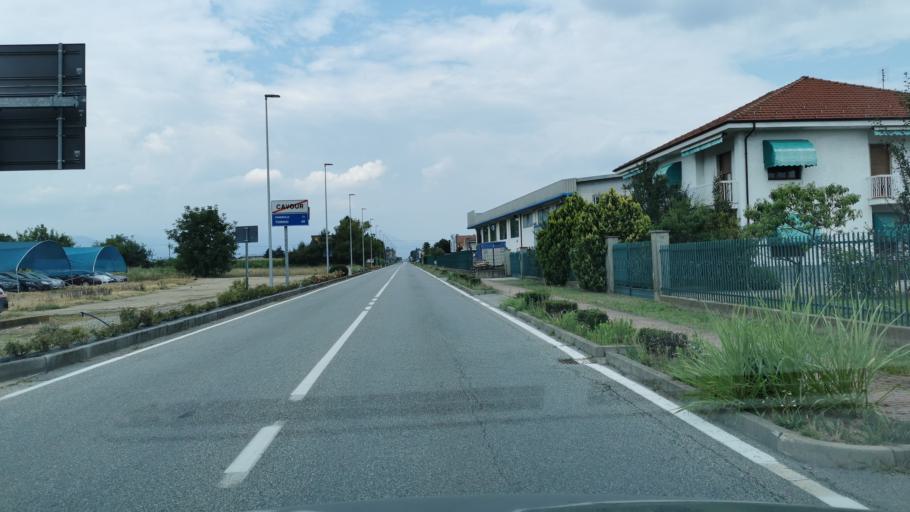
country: IT
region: Piedmont
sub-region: Provincia di Torino
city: Cavour
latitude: 44.7946
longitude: 7.3747
